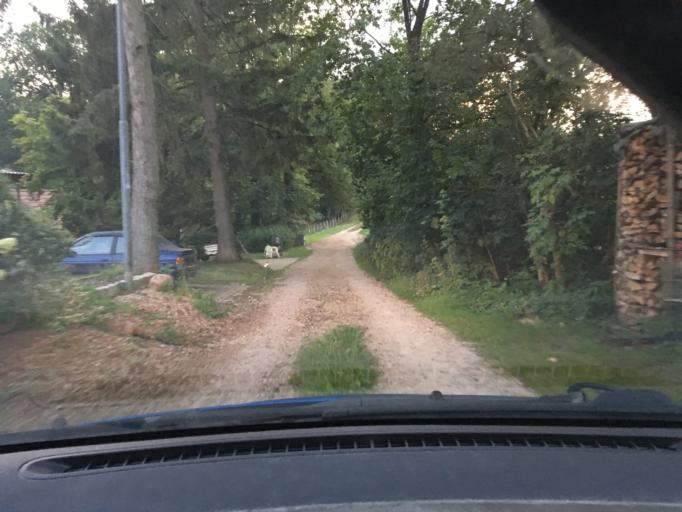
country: DE
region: Lower Saxony
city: Thomasburg
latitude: 53.1887
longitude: 10.6235
